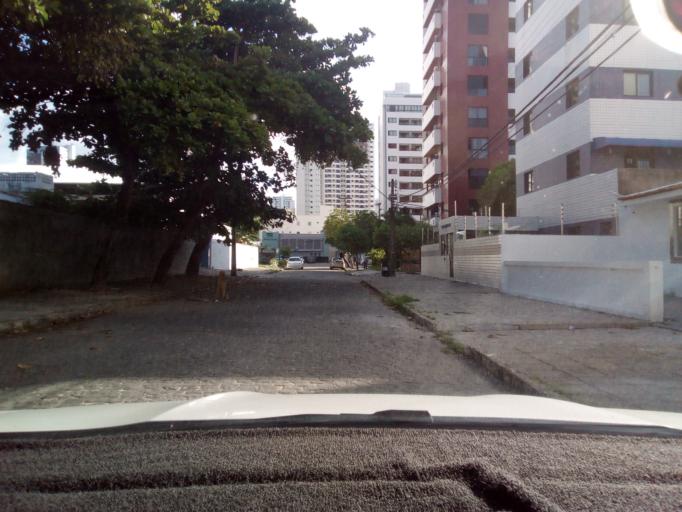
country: BR
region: Paraiba
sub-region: Joao Pessoa
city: Joao Pessoa
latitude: -7.1105
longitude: -34.8283
